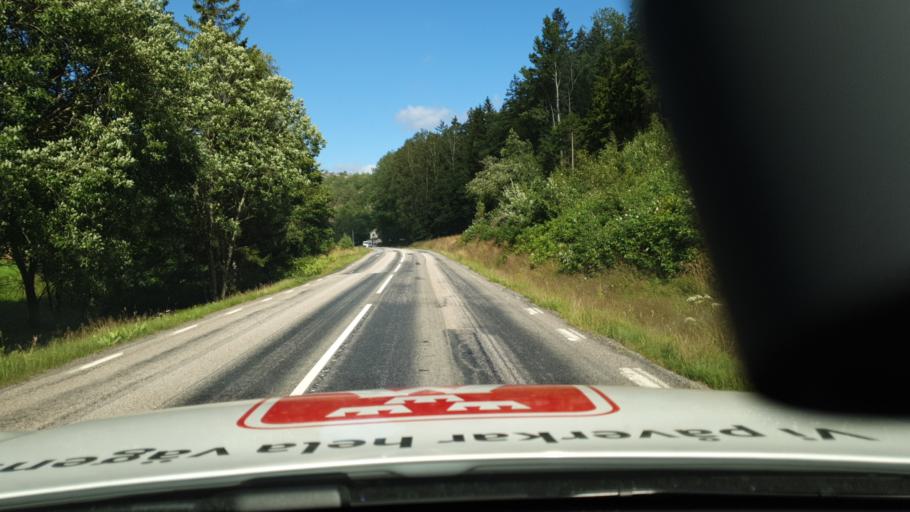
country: SE
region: Vaestra Goetaland
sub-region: Orust
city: Henan
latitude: 58.2214
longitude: 11.6011
